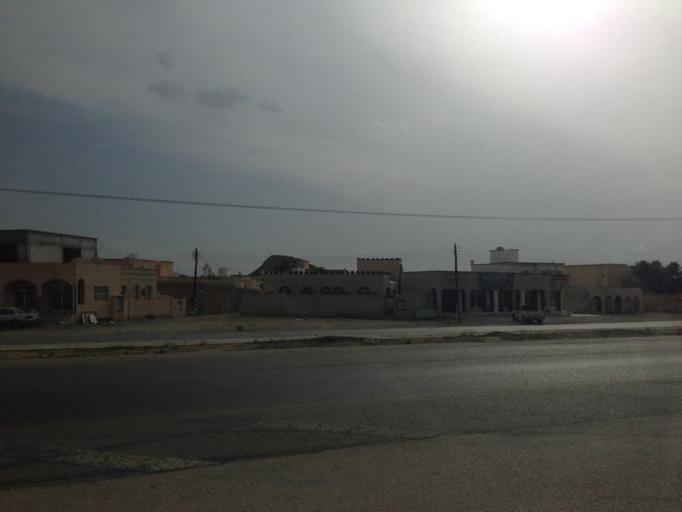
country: OM
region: Ash Sharqiyah
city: Al Qabil
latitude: 22.5872
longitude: 58.6835
